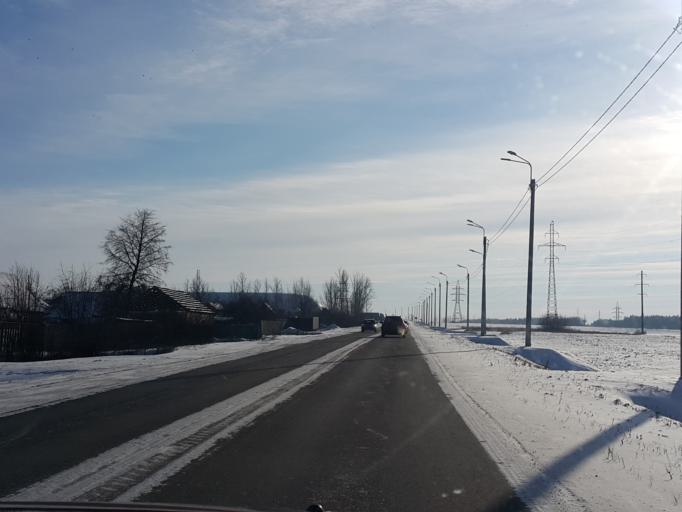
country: RU
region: Tambov
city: Znamenka
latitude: 52.4306
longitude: 41.4995
